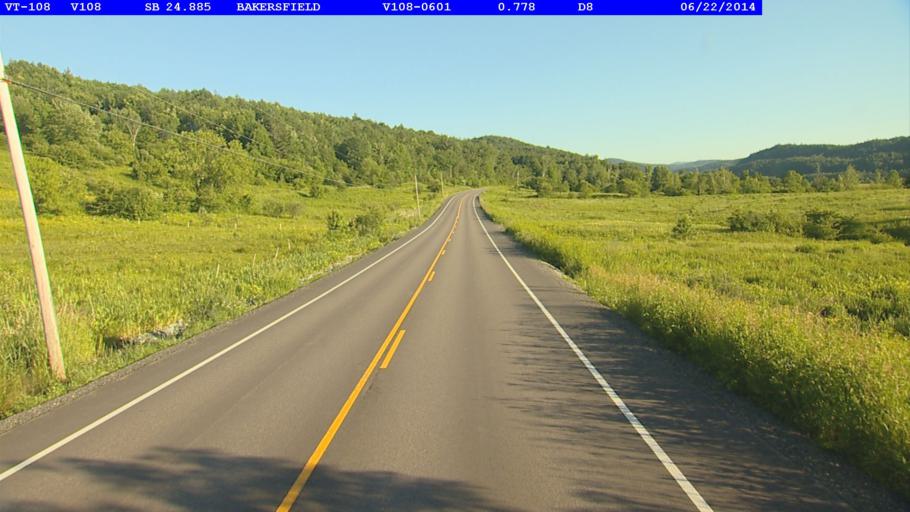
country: US
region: Vermont
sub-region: Franklin County
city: Enosburg Falls
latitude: 44.7443
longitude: -72.8234
